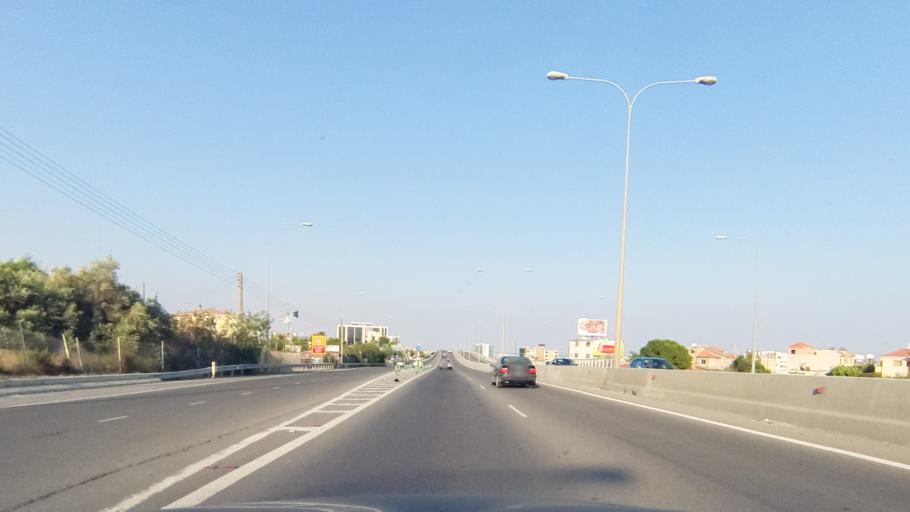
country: CY
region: Limassol
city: Limassol
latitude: 34.7053
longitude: 33.0409
